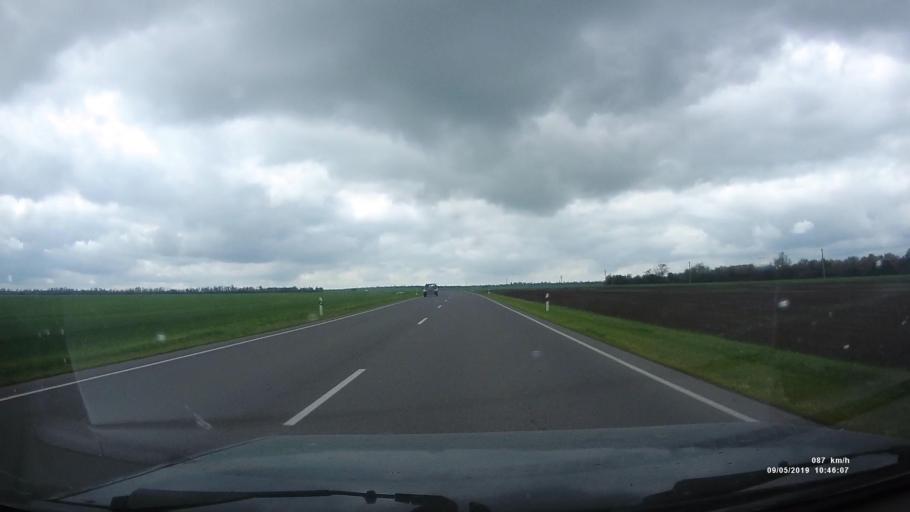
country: RU
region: Rostov
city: Peshkovo
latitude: 46.9884
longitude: 39.3585
